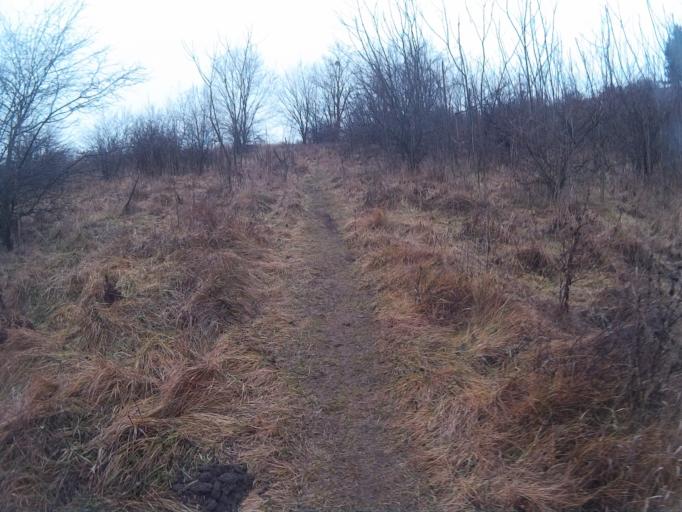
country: HU
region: Komarom-Esztergom
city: Tokod
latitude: 47.7130
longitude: 18.6482
